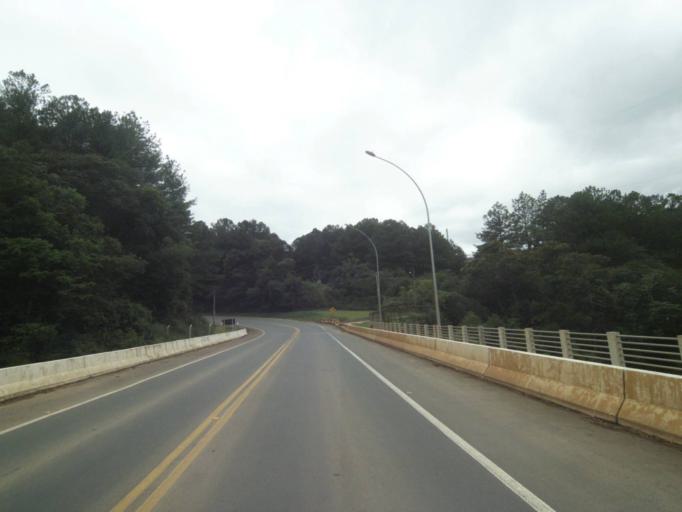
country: BR
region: Parana
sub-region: Telemaco Borba
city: Telemaco Borba
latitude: -24.3124
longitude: -50.6150
